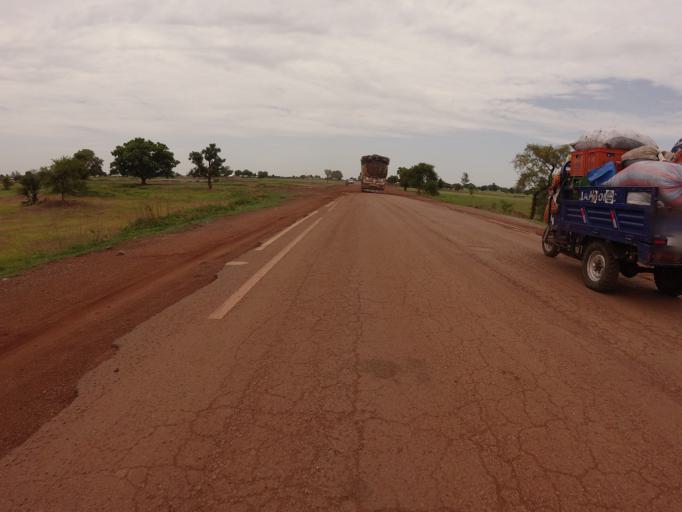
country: GH
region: Upper East
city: Bawku
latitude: 11.0024
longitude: -0.3796
